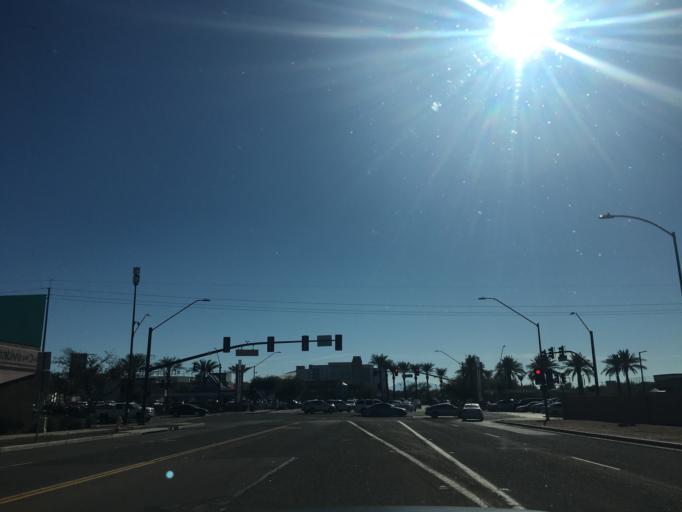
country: US
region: Arizona
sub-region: Maricopa County
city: Peoria
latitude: 33.5381
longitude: -112.2638
